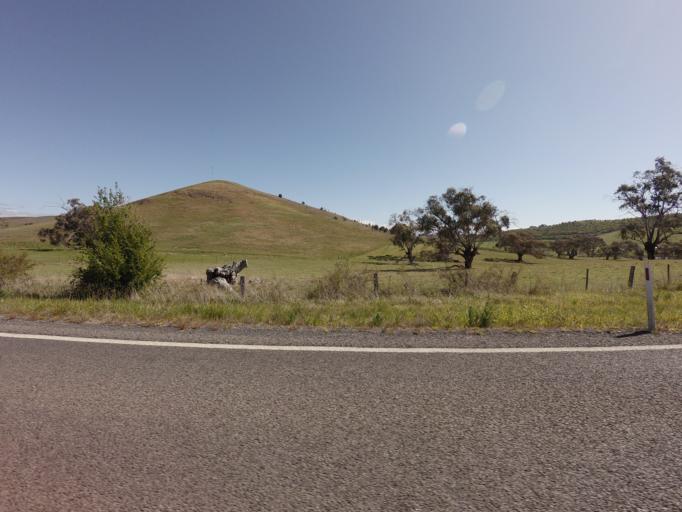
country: AU
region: Tasmania
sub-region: Derwent Valley
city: New Norfolk
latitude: -42.5719
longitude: 146.8817
